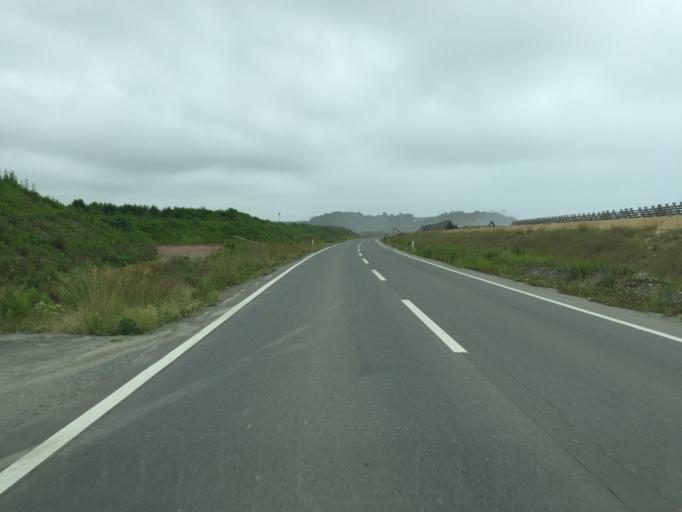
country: JP
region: Fukushima
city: Namie
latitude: 37.7176
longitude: 141.0094
